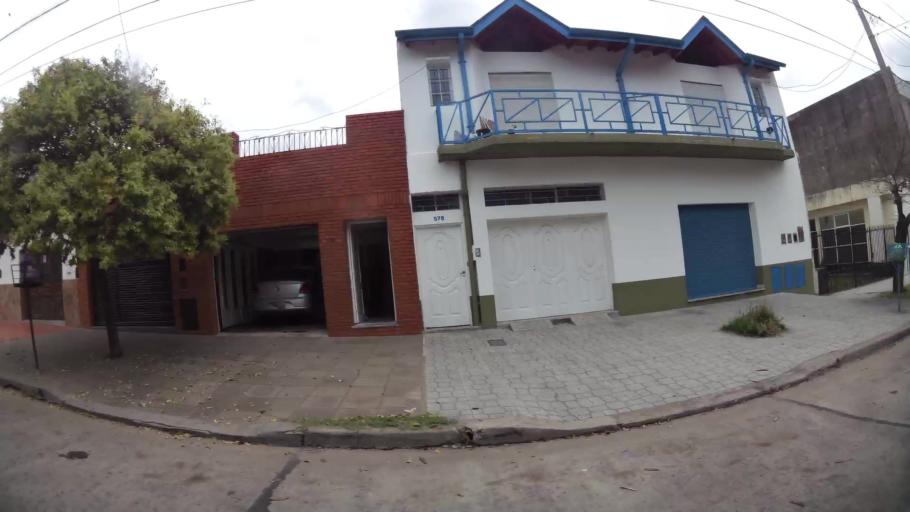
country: AR
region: Buenos Aires
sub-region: Partido de Campana
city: Campana
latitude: -34.1703
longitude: -58.9547
